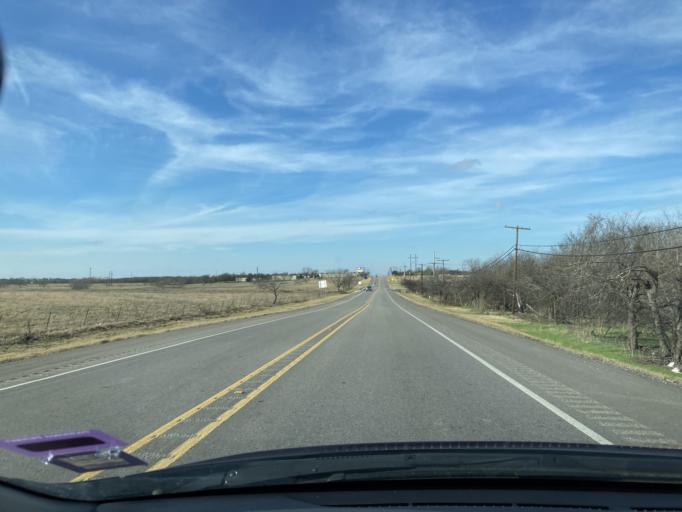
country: US
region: Texas
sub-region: Navarro County
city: Corsicana
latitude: 32.0581
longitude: -96.4300
